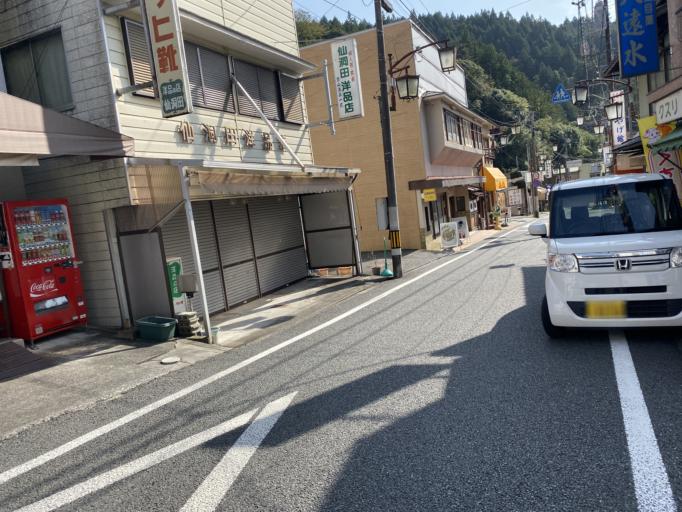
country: JP
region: Shizuoka
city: Fujinomiya
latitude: 35.3771
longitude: 138.4249
